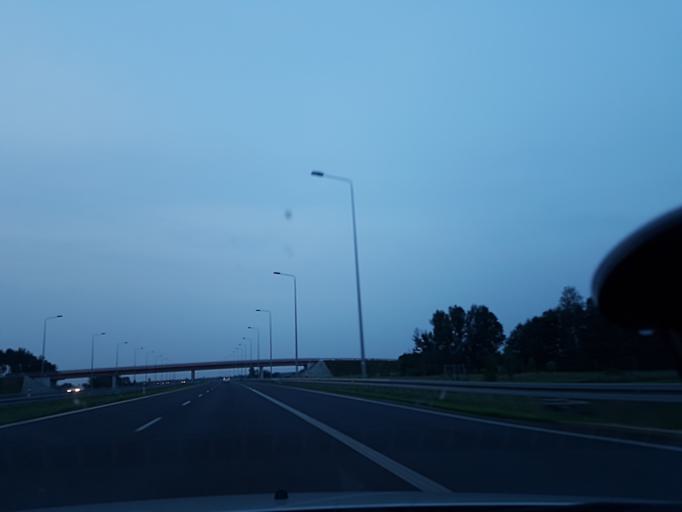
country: PL
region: Lodz Voivodeship
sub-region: Powiat leczycki
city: Piatek
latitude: 52.0050
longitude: 19.5439
